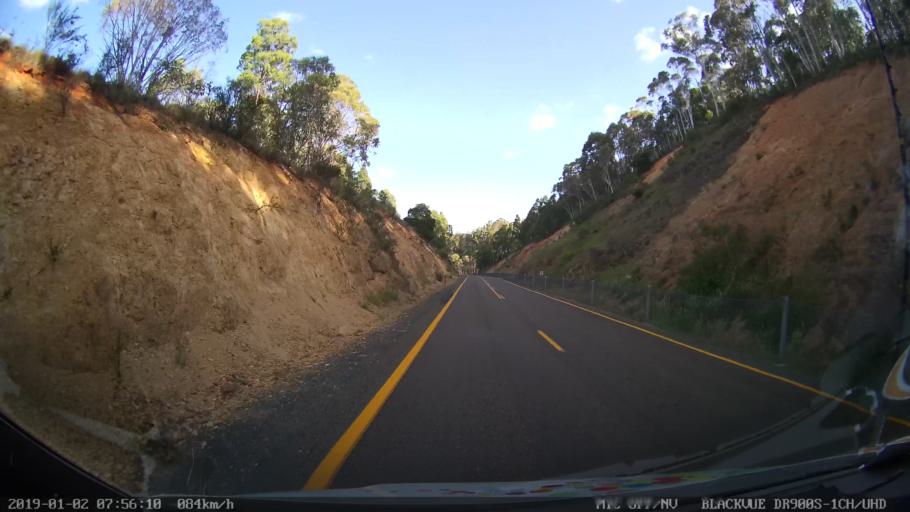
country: AU
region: New South Wales
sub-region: Tumut Shire
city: Tumut
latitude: -35.6740
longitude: 148.4859
